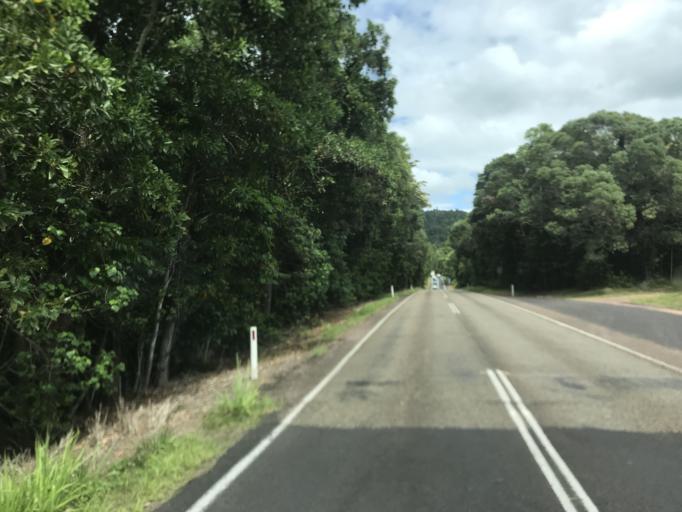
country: AU
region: Queensland
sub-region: Cassowary Coast
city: Innisfail
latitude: -17.8688
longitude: 146.0842
